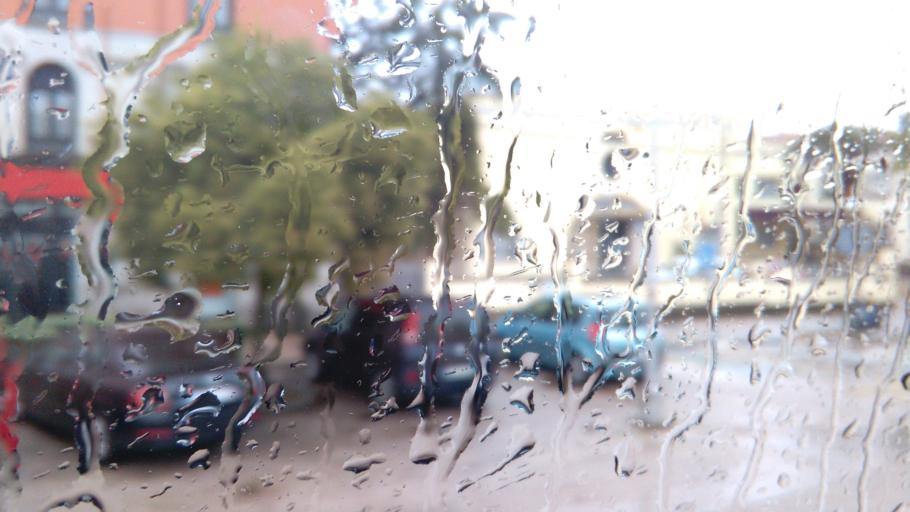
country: ES
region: Extremadura
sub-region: Provincia de Caceres
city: Trujillo
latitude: 39.4569
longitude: -5.8828
